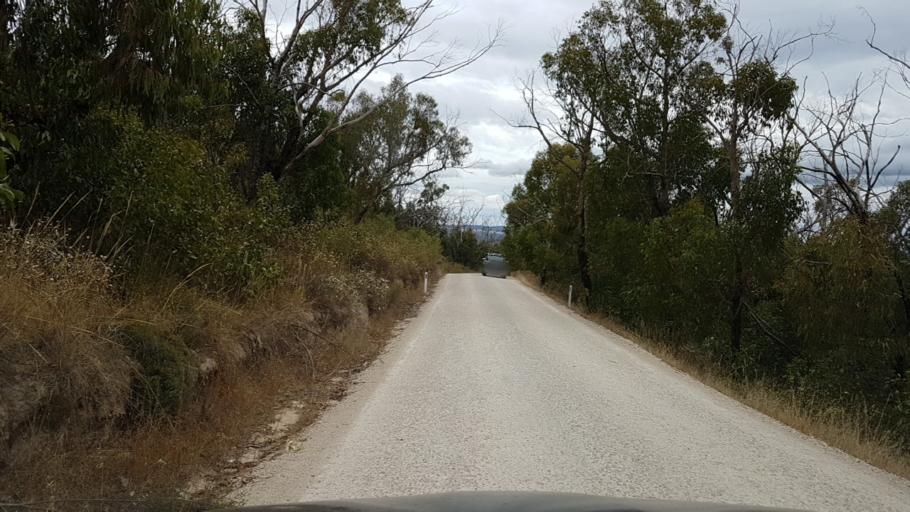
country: AU
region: South Australia
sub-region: Tea Tree Gully
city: Golden Grove
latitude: -34.7741
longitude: 138.8149
